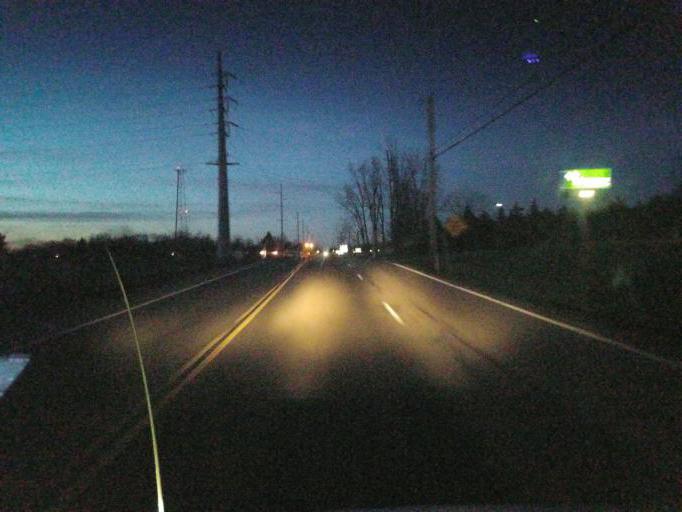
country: US
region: Ohio
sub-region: Logan County
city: Bellefontaine
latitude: 40.3838
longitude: -83.7536
